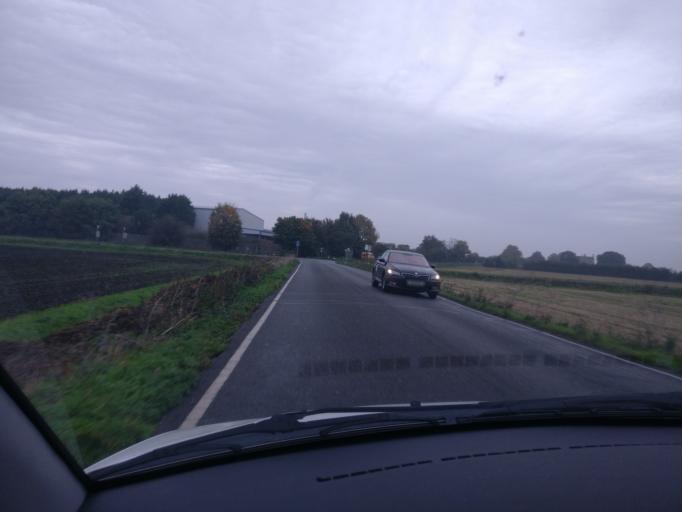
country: GB
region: England
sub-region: Peterborough
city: Eye
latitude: 52.5886
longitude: -0.1936
